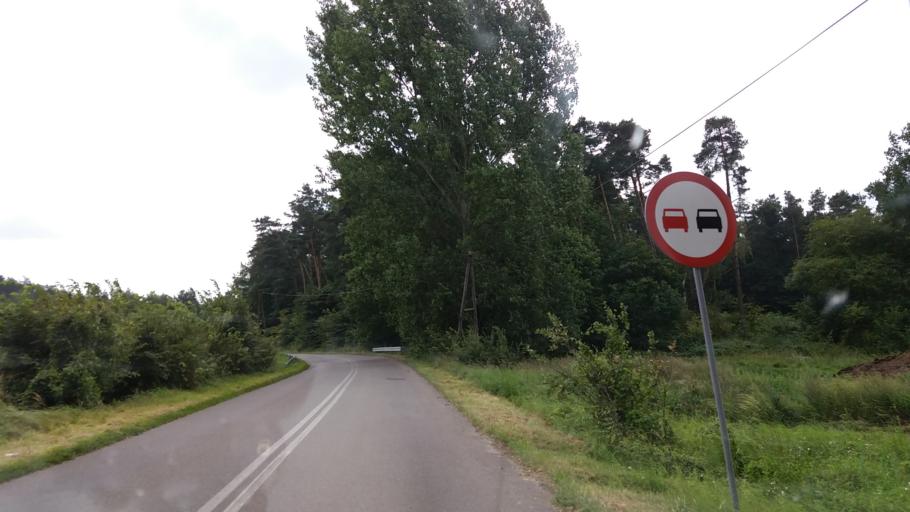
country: PL
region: West Pomeranian Voivodeship
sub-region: Powiat choszczenski
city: Krzecin
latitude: 53.0906
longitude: 15.4738
